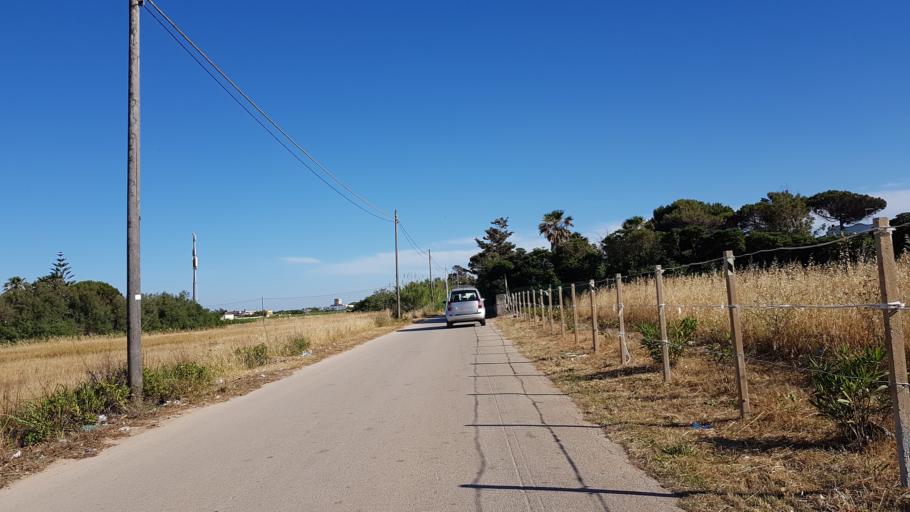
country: IT
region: Apulia
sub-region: Provincia di Brindisi
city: Brindisi
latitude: 40.6827
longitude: 17.8751
